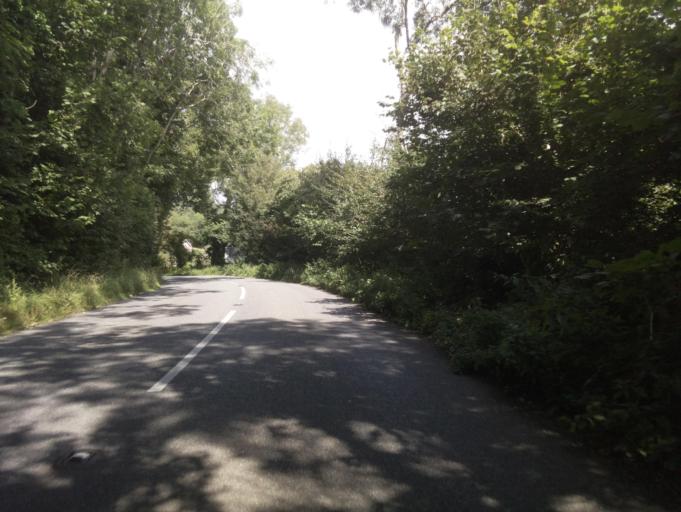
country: GB
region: England
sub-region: Devon
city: Dartmouth
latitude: 50.3579
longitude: -3.5617
